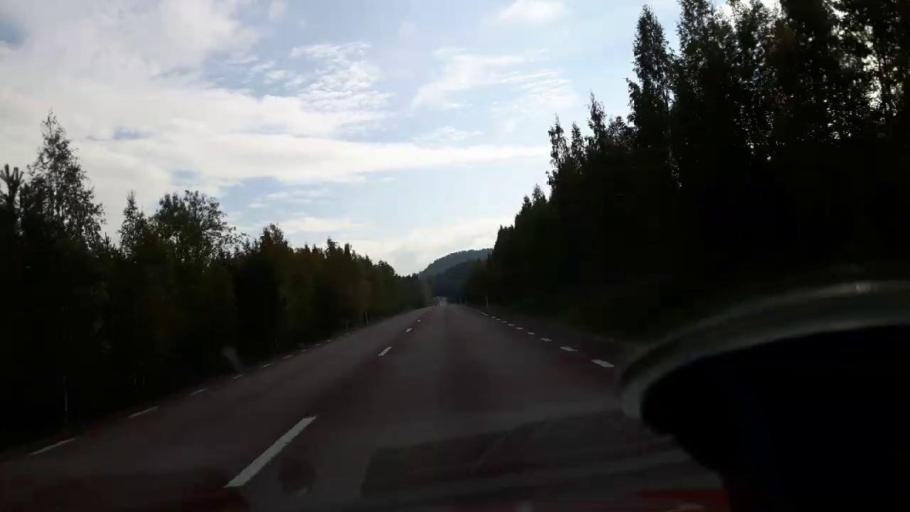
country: SE
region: Gaevleborg
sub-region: Bollnas Kommun
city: Kilafors
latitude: 61.2123
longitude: 16.7380
